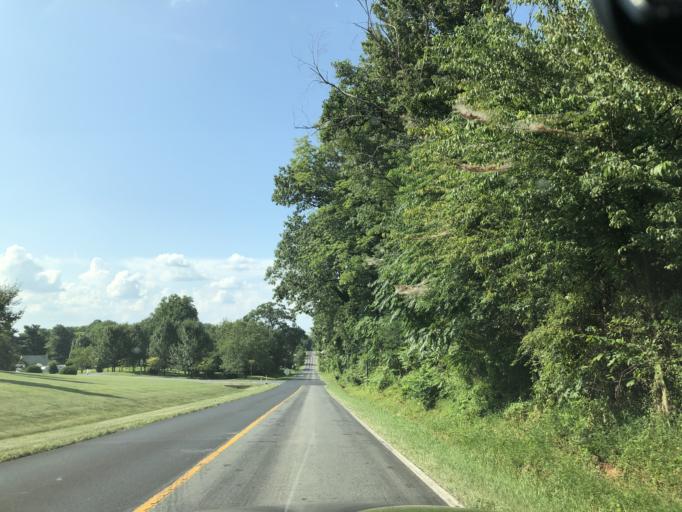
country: US
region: Maryland
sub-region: Frederick County
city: Linganore
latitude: 39.4183
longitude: -77.1761
